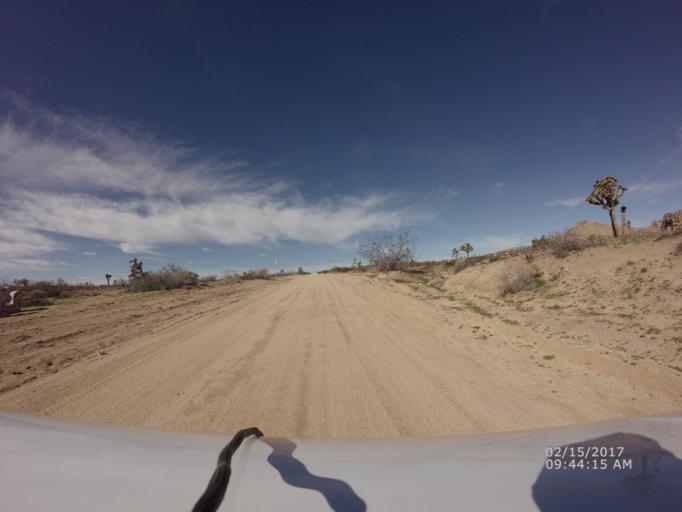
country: US
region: California
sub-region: Los Angeles County
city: Lake Los Angeles
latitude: 34.6239
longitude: -117.8912
